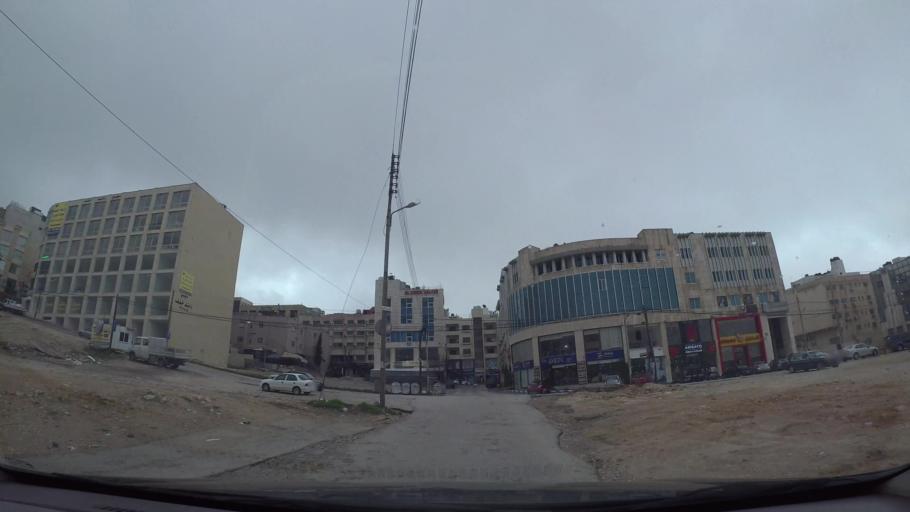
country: JO
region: Amman
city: Wadi as Sir
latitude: 31.9571
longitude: 35.8632
